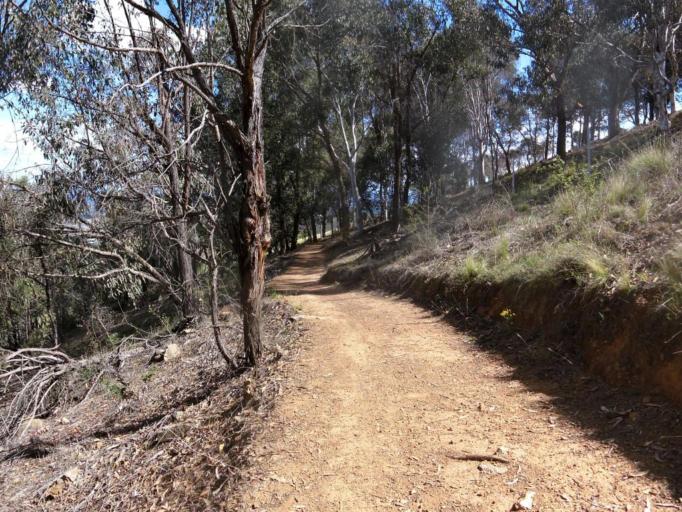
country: AU
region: Australian Capital Territory
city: Belconnen
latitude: -35.1451
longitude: 149.0921
